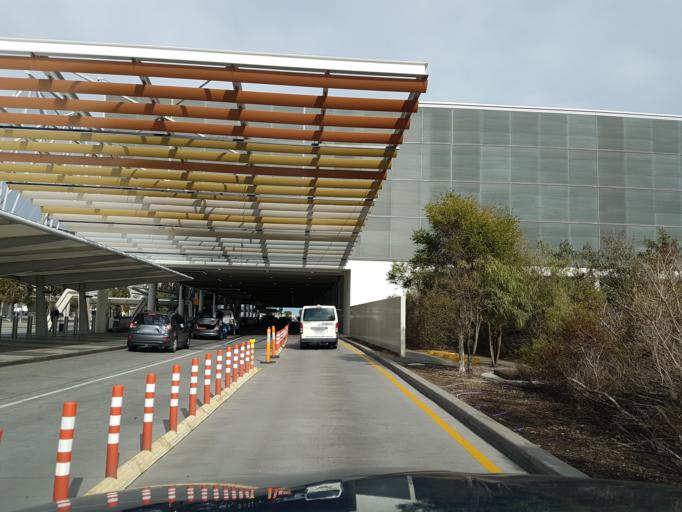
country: AU
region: South Australia
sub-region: City of West Torrens
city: Plympton
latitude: -34.9372
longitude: 138.5374
